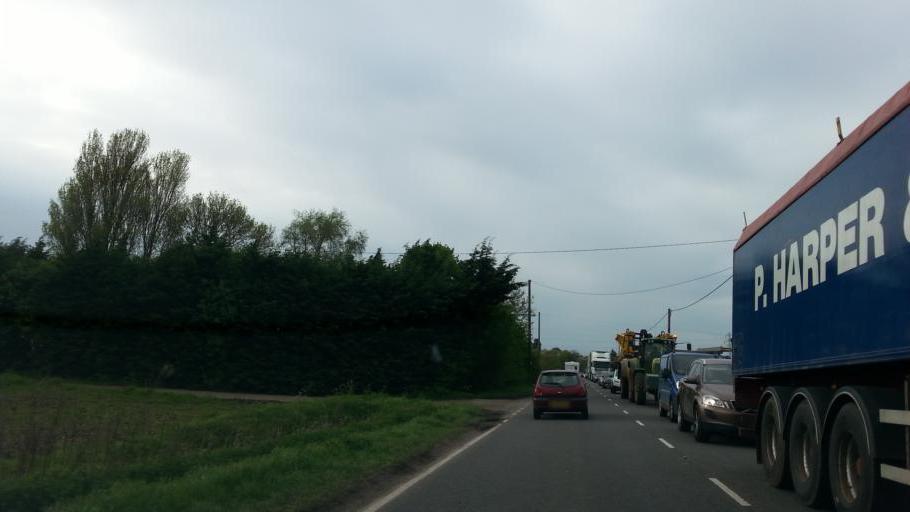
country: GB
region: England
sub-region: Cambridgeshire
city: March
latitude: 52.5708
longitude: 0.0591
